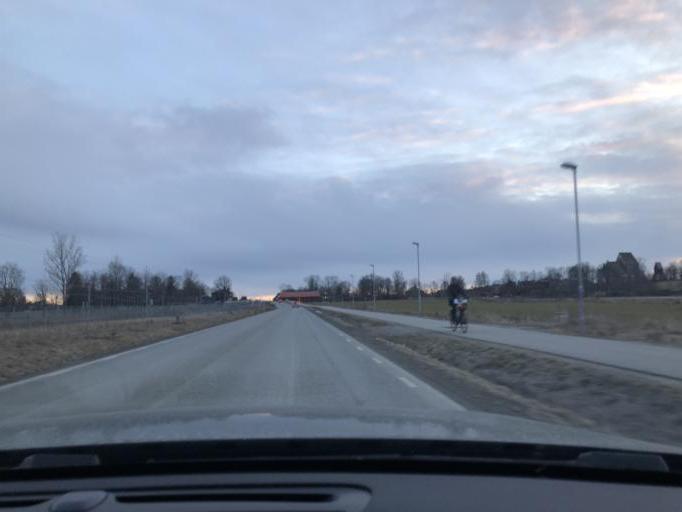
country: SE
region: Uppsala
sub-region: Uppsala Kommun
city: Gamla Uppsala
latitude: 59.9025
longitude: 17.6410
